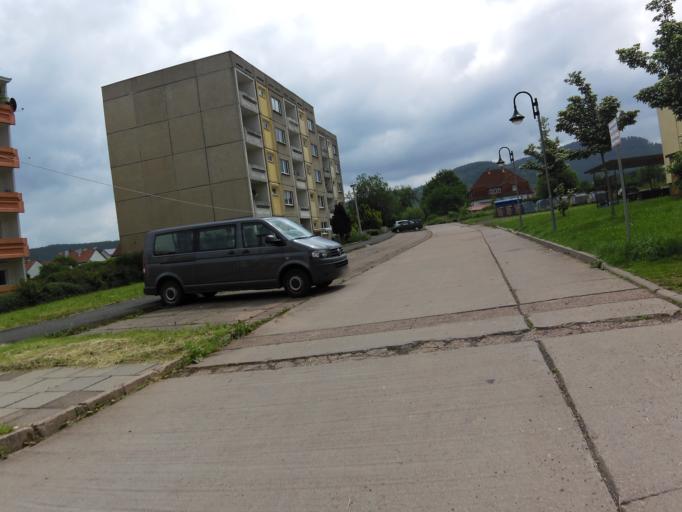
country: DE
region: Thuringia
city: Tabarz
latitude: 50.8826
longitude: 10.5068
